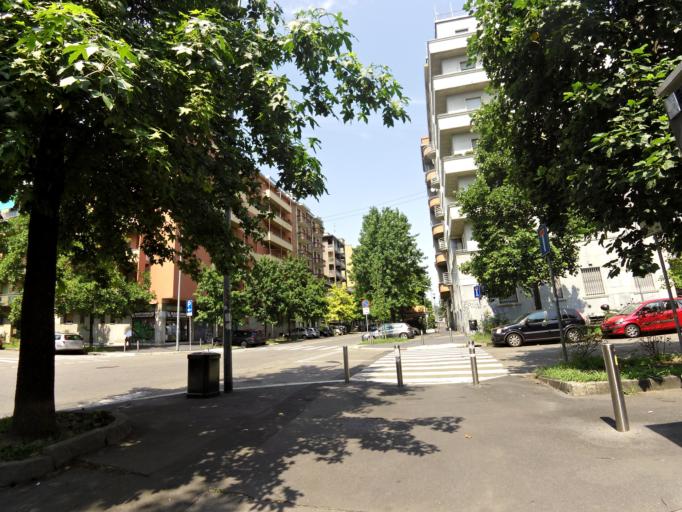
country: IT
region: Lombardy
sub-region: Citta metropolitana di Milano
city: Milano
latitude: 45.4815
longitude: 9.1456
